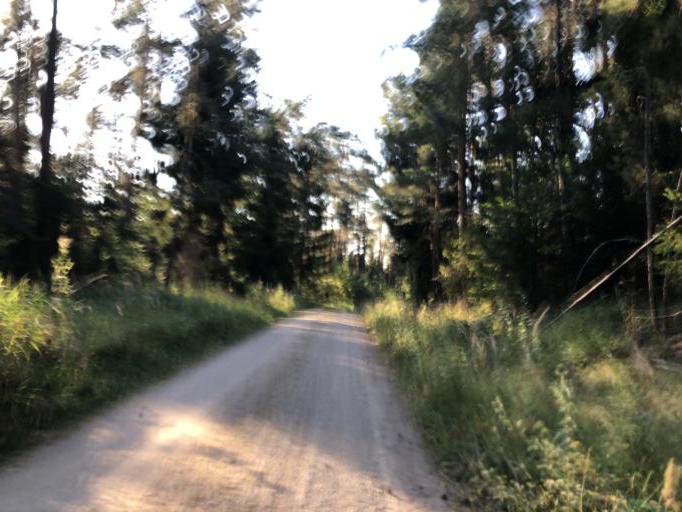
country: DE
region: Bavaria
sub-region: Regierungsbezirk Mittelfranken
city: Uttenreuth
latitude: 49.5622
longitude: 11.0861
